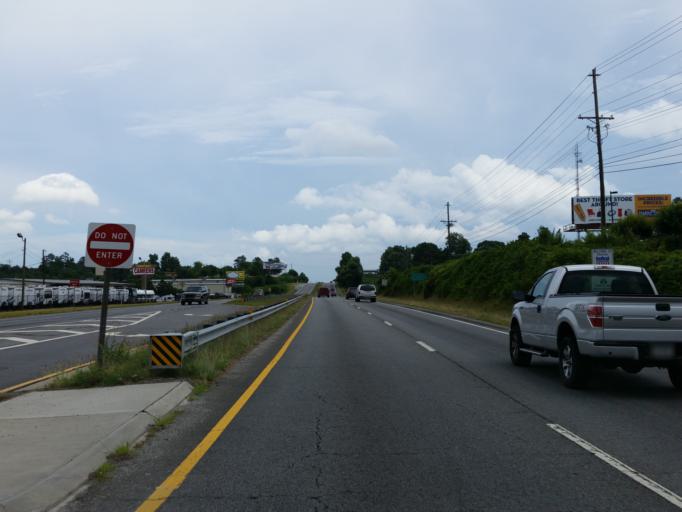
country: US
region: Georgia
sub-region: Cobb County
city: Marietta
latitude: 33.9861
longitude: -84.5693
